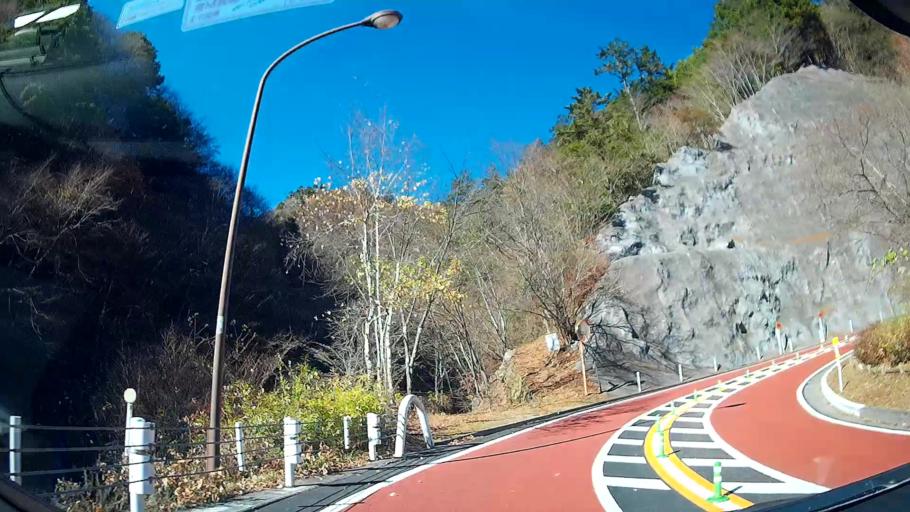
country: JP
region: Yamanashi
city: Uenohara
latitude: 35.7352
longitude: 139.0305
